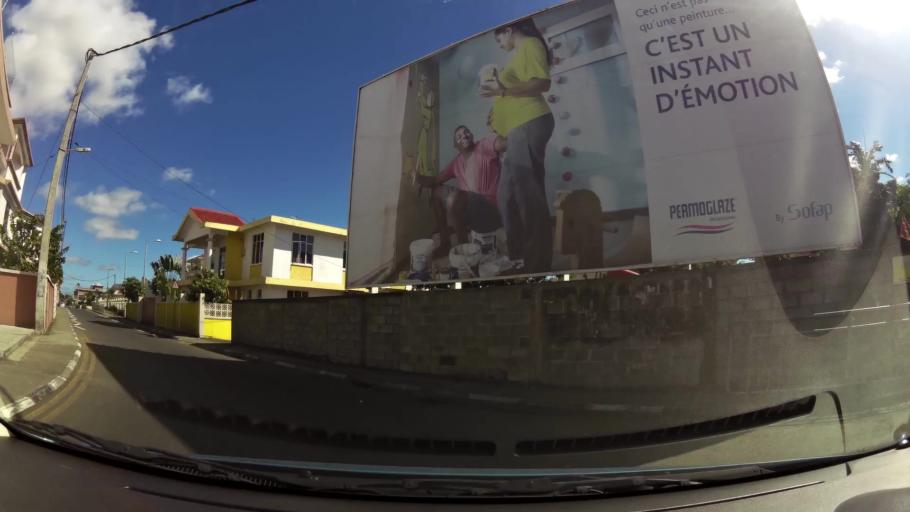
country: MU
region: Plaines Wilhems
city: Vacoas
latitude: -20.2851
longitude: 57.4800
